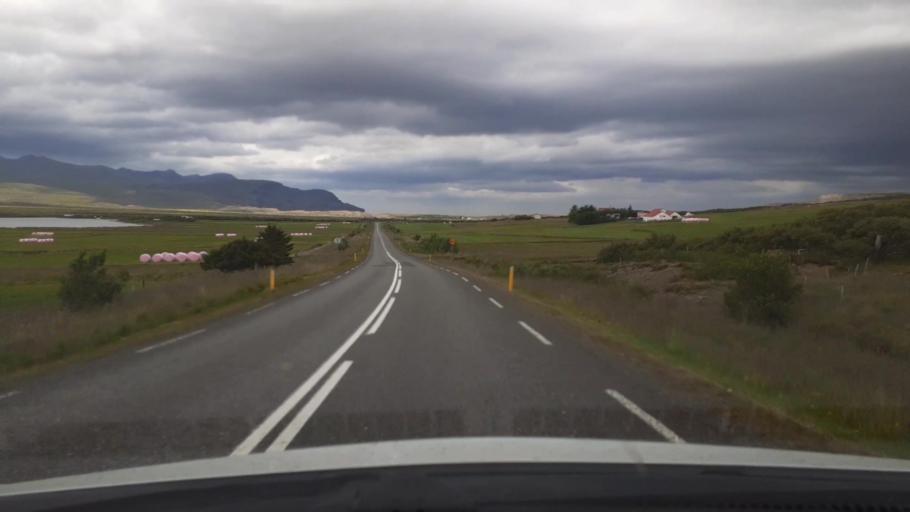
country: IS
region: West
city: Borgarnes
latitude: 64.5442
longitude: -21.5949
